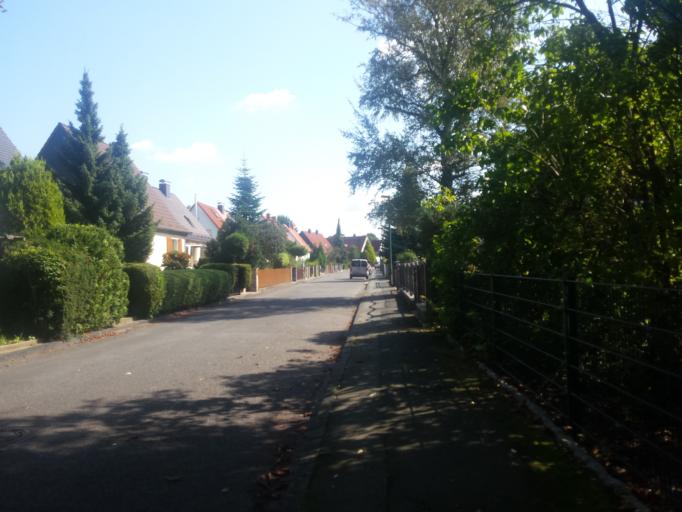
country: DE
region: Saxony
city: Taucha
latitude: 51.3494
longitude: 12.4420
